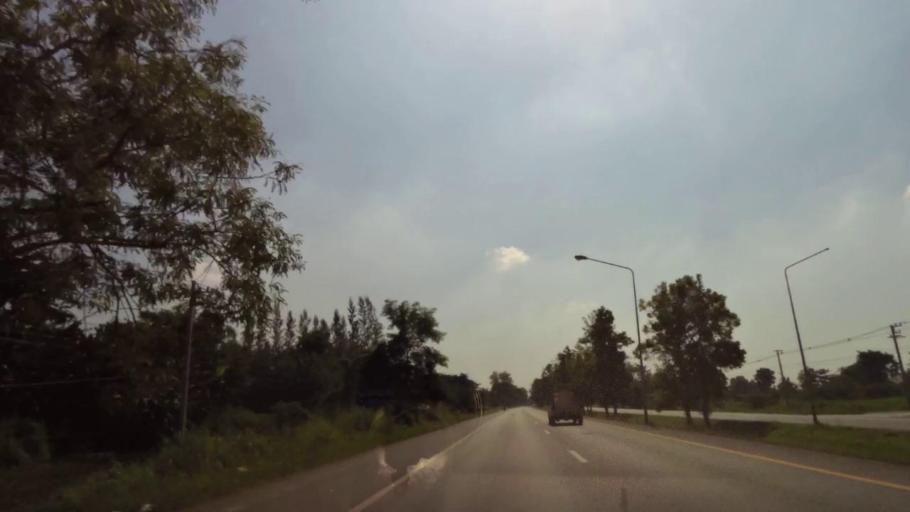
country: TH
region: Phichit
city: Bueng Na Rang
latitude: 16.1847
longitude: 100.1287
